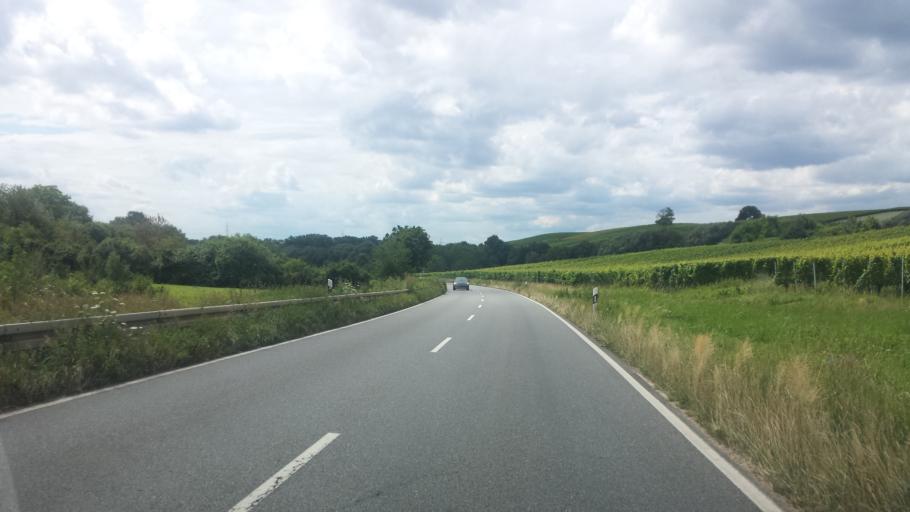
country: DE
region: Baden-Wuerttemberg
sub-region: Karlsruhe Region
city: Rauenberg
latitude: 49.2784
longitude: 8.7149
